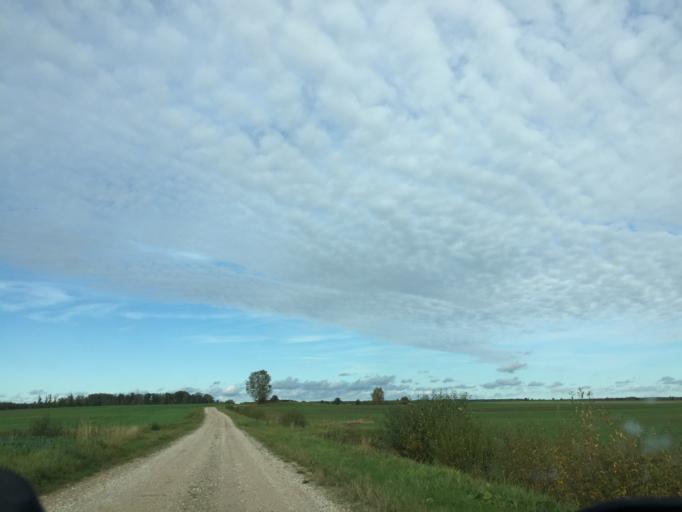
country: LV
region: Jaunpils
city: Jaunpils
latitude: 56.6495
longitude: 23.0784
